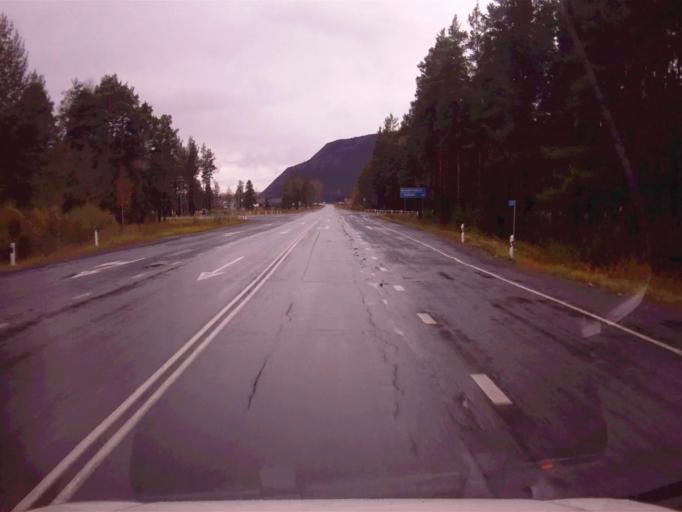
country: RU
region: Chelyabinsk
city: Verkhniy Ufaley
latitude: 56.0288
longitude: 60.2851
